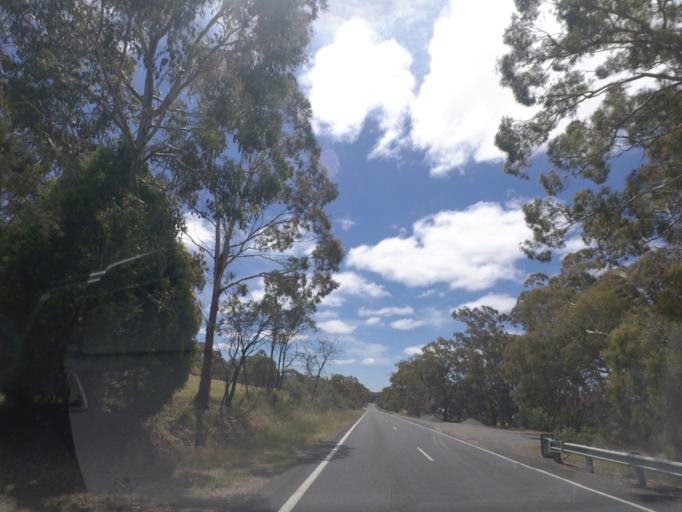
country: AU
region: Victoria
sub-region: Mount Alexander
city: Castlemaine
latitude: -37.2970
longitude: 144.1625
